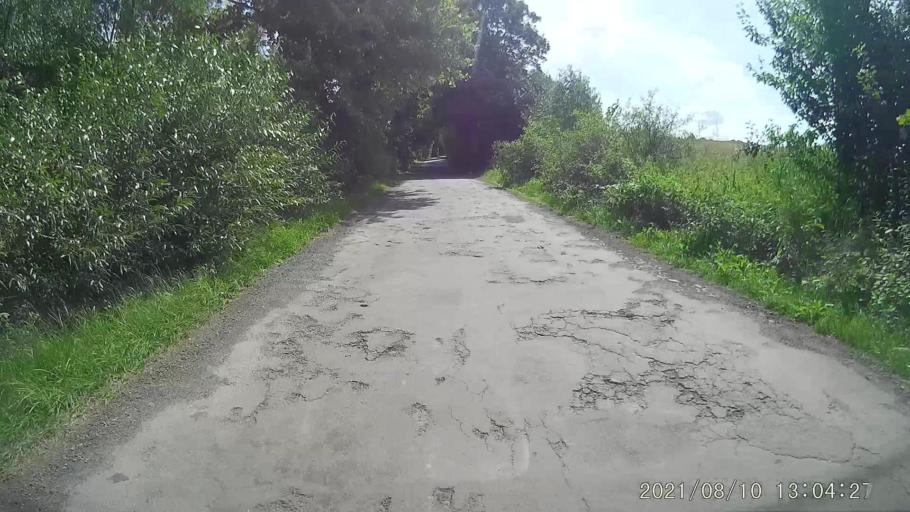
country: PL
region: Lower Silesian Voivodeship
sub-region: Powiat klodzki
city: Bozkow
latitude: 50.4769
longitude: 16.5640
